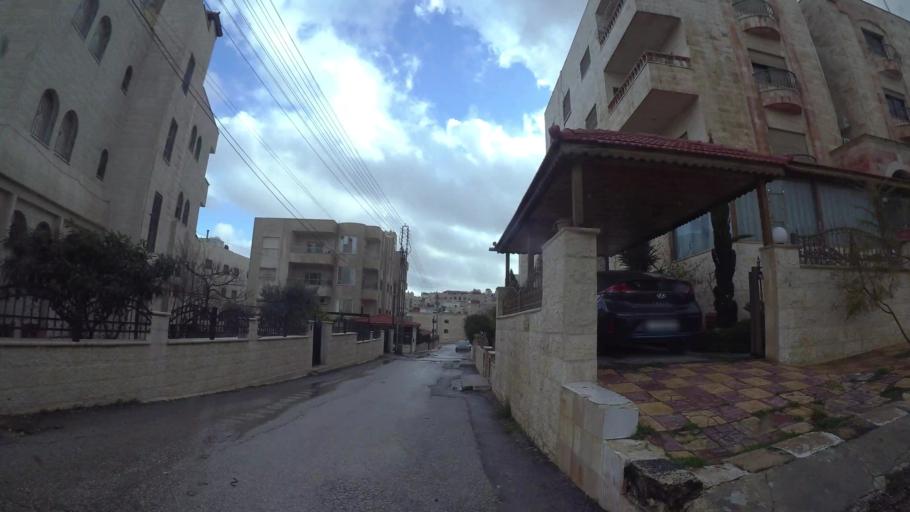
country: JO
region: Amman
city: Al Jubayhah
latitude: 32.0342
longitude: 35.8674
